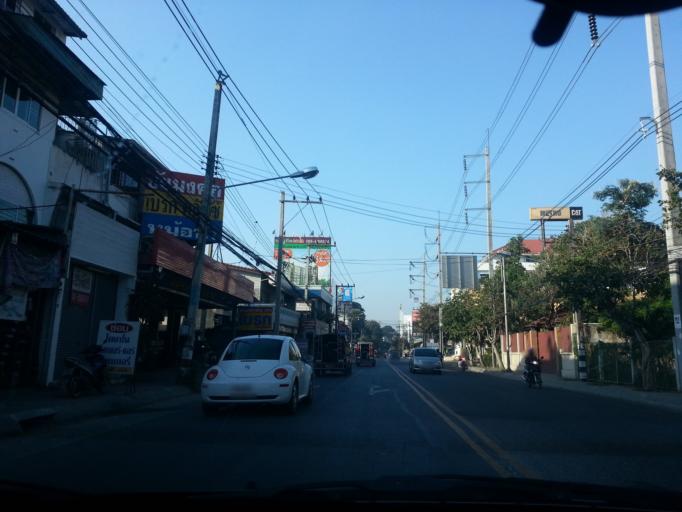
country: TH
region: Chiang Mai
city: Chiang Mai
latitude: 18.8013
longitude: 99.0146
